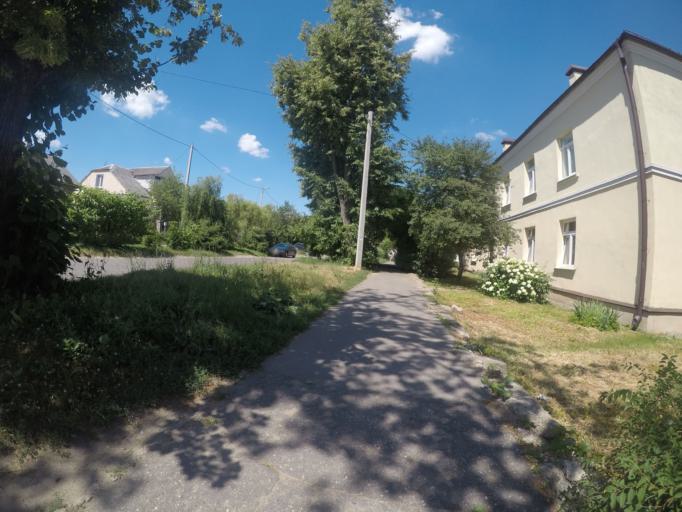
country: BY
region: Grodnenskaya
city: Hrodna
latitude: 53.6918
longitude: 23.8298
